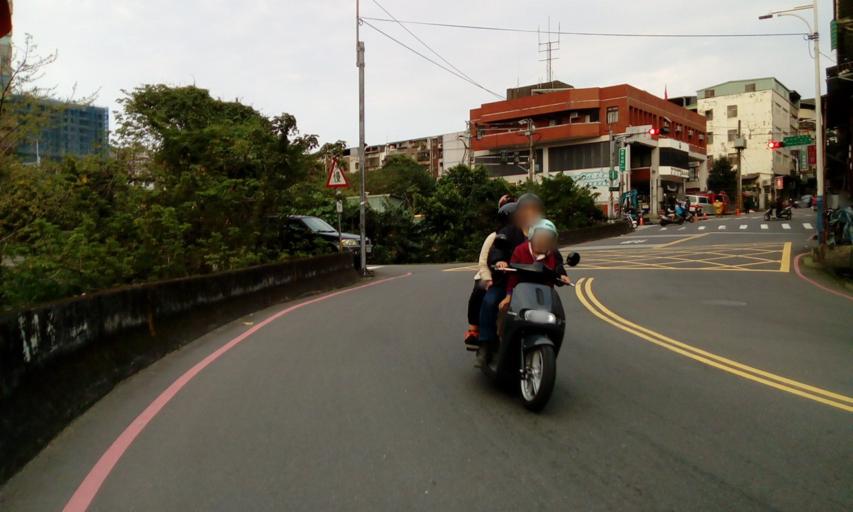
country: TW
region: Taipei
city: Taipei
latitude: 25.1747
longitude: 121.4390
